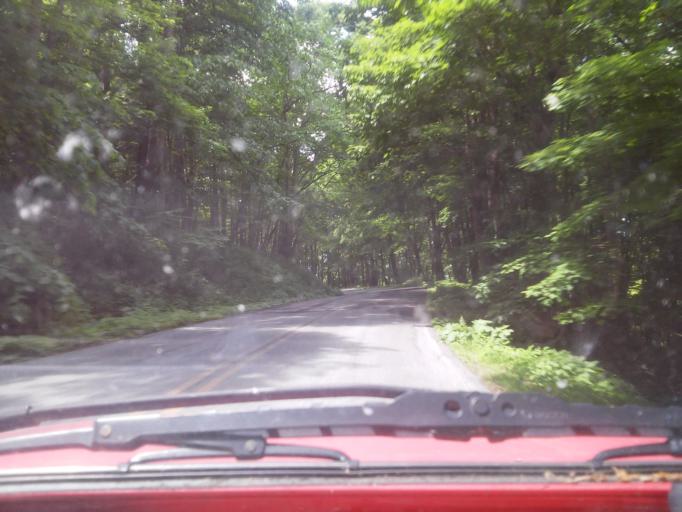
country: US
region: Virginia
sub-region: Giles County
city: Pembroke
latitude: 37.3412
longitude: -80.5521
